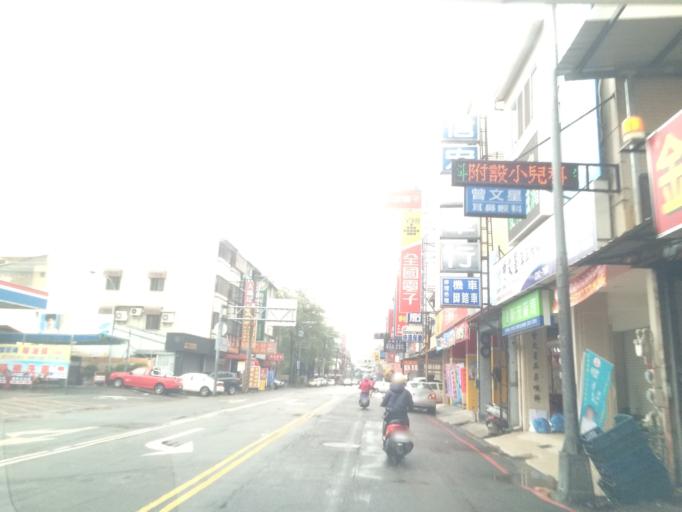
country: TW
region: Taiwan
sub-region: Taichung City
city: Taichung
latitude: 24.1818
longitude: 120.6886
